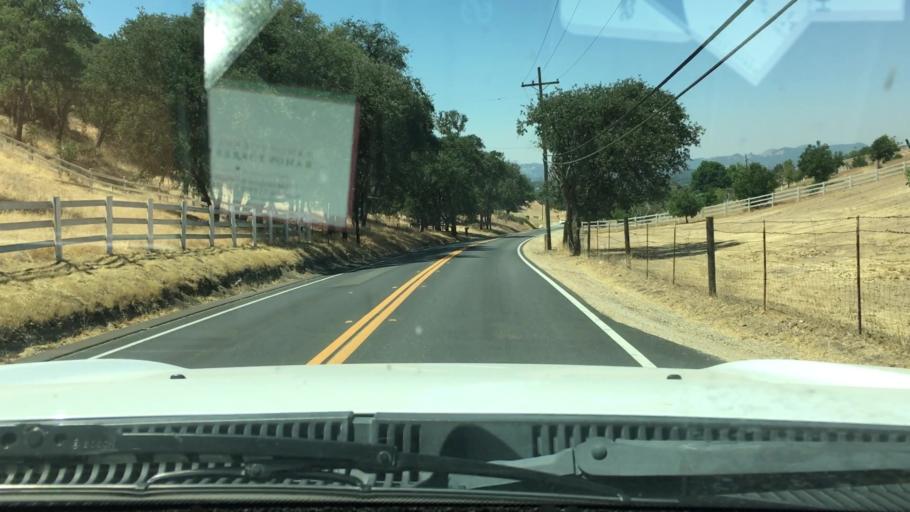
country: US
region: California
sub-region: San Luis Obispo County
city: Atascadero
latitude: 35.5086
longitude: -120.6410
